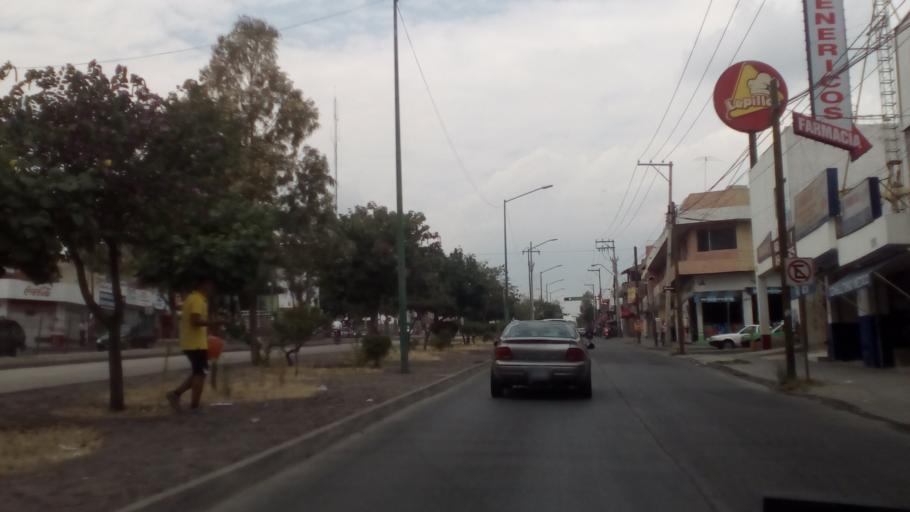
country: MX
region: Guanajuato
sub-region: Leon
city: La Ermita
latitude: 21.1314
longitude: -101.7060
